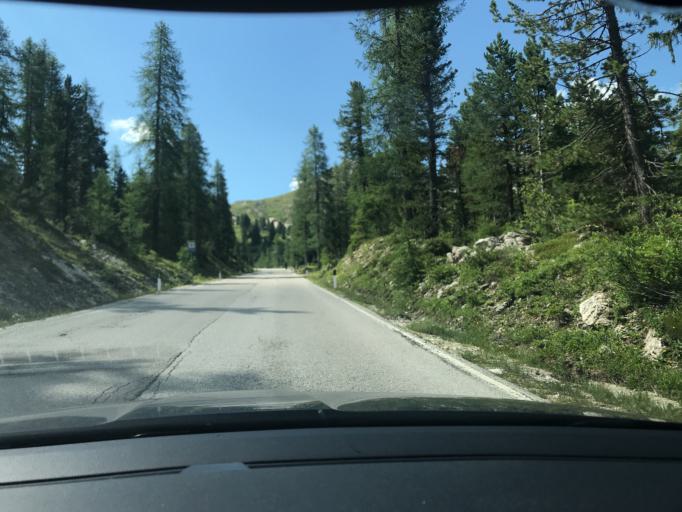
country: IT
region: Veneto
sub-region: Provincia di Belluno
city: Livinallongo del Col di Lana
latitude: 46.5390
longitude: 11.9846
